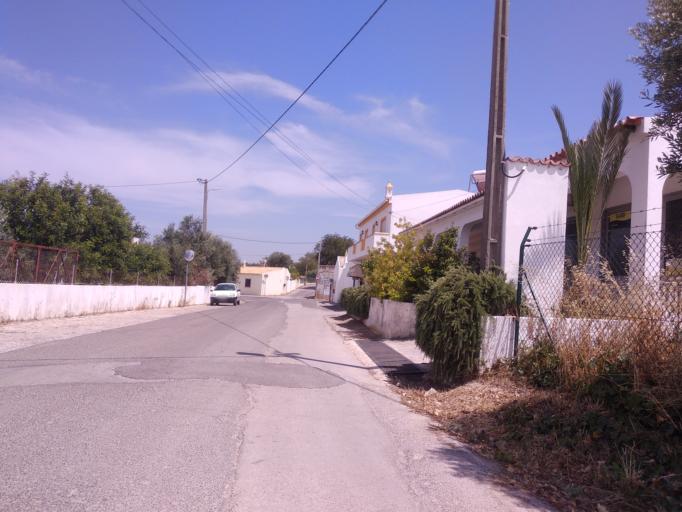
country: PT
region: Faro
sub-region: Faro
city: Santa Barbara de Nexe
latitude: 37.1212
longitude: -7.9431
